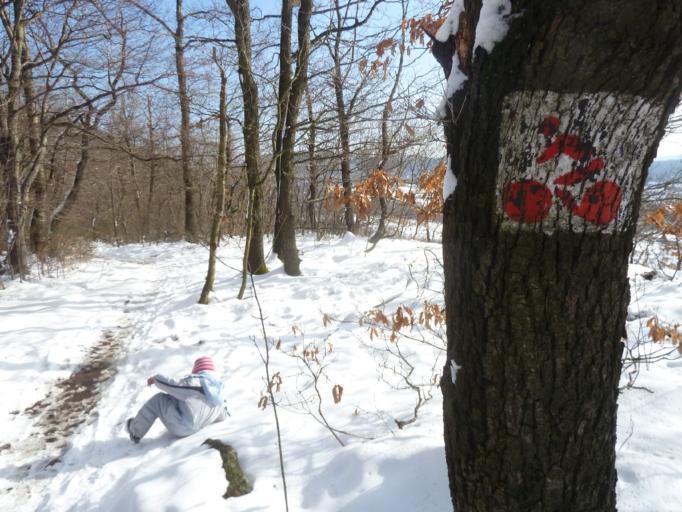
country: HU
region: Pest
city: Pilisborosjeno
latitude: 47.5734
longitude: 18.9757
